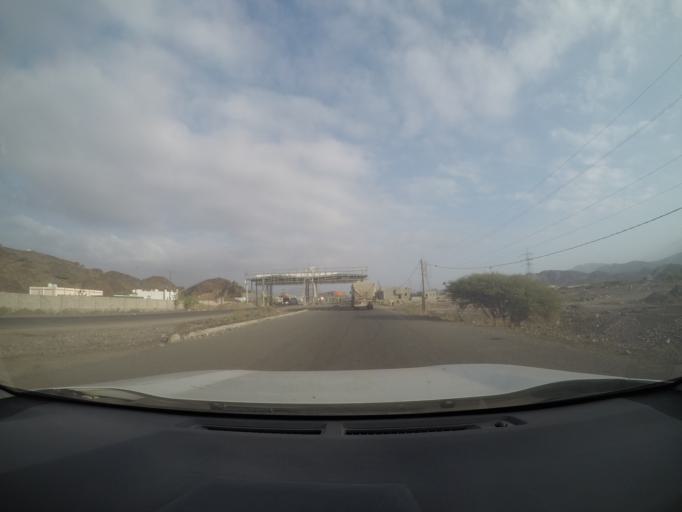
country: YE
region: Lahij
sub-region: Al Milah
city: Al Milah
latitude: 13.2841
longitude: 44.7564
